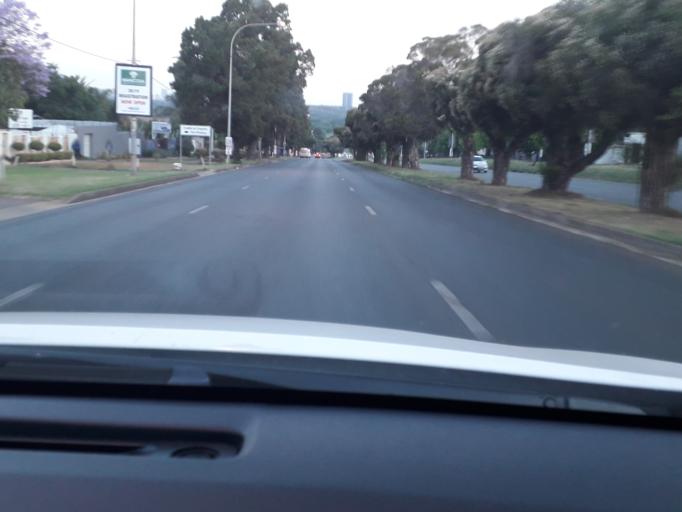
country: ZA
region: Gauteng
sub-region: City of Johannesburg Metropolitan Municipality
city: Johannesburg
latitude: -26.1475
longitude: 27.9862
